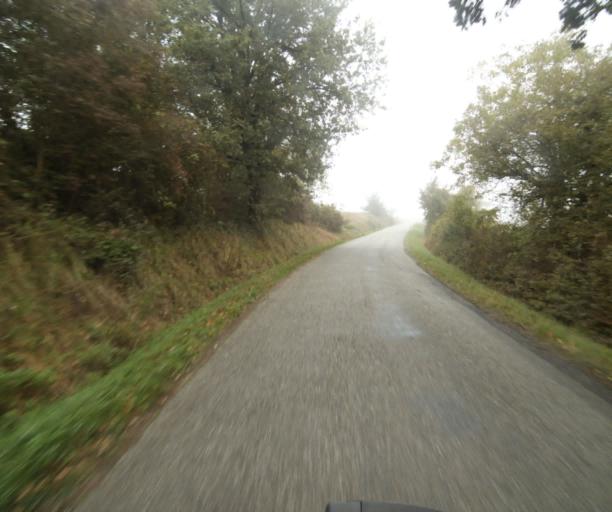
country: FR
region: Midi-Pyrenees
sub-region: Departement de la Haute-Garonne
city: Villemur-sur-Tarn
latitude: 43.8974
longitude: 1.4926
